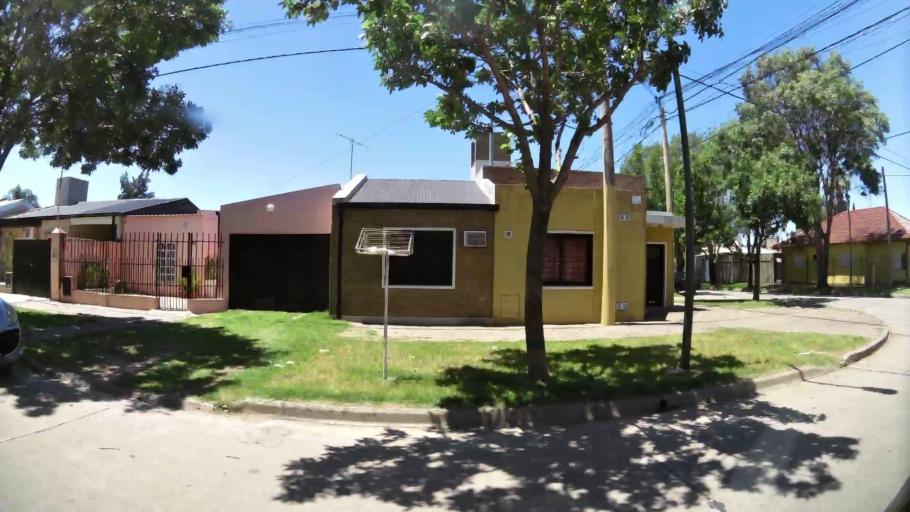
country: AR
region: Santa Fe
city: Rafaela
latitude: -31.2533
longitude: -61.4593
